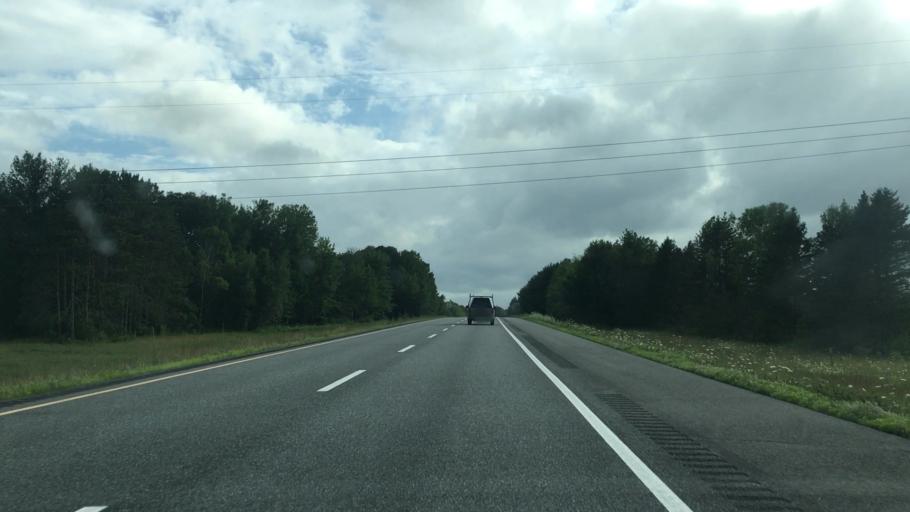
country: US
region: Maine
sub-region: Kennebec County
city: Benton
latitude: 44.6085
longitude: -69.5725
